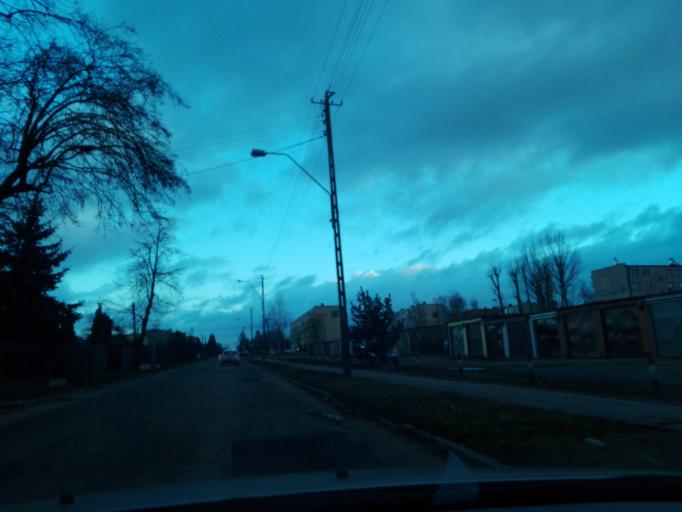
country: PL
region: Lodz Voivodeship
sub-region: Powiat kutnowski
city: Kutno
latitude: 52.2436
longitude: 19.3578
